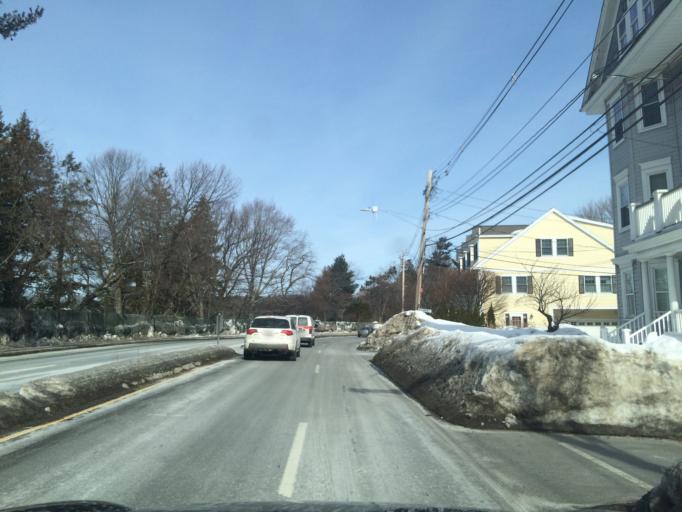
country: US
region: Massachusetts
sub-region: Suffolk County
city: Jamaica Plain
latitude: 42.3116
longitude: -71.1426
